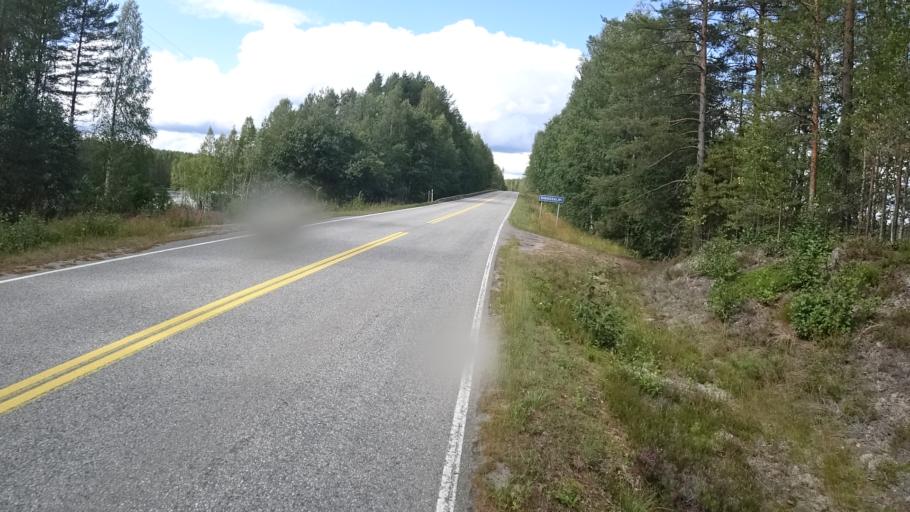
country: FI
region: North Karelia
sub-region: Joensuu
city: Ilomantsi
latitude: 62.6182
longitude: 31.2038
